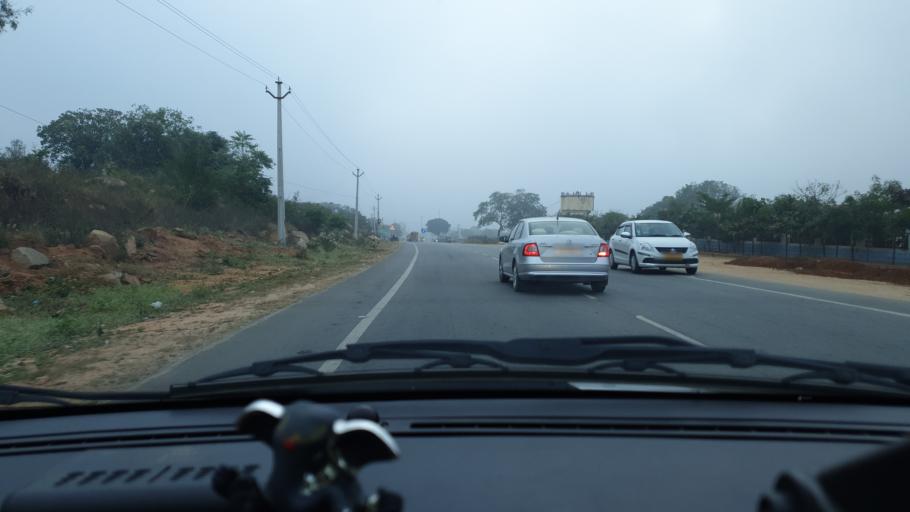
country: IN
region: Telangana
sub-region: Mahbubnagar
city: Farrukhnagar
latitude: 16.9564
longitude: 78.5145
